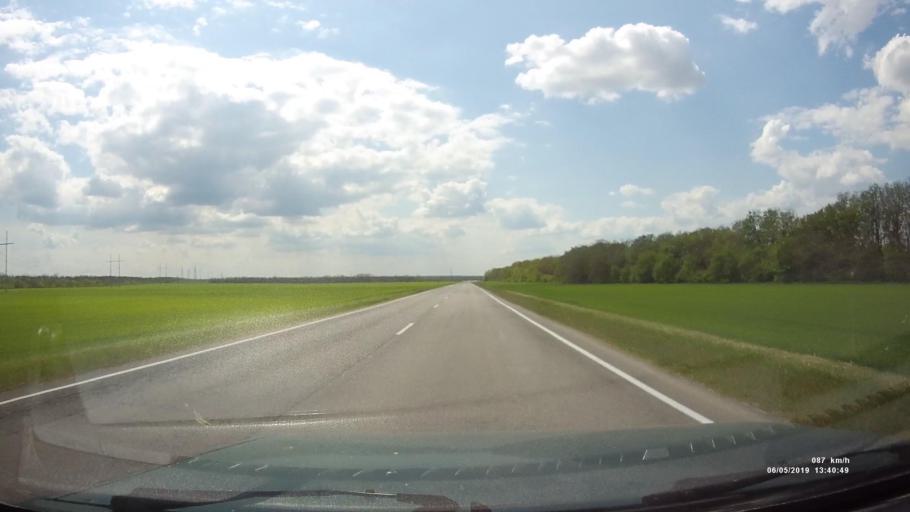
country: RU
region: Rostov
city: Ust'-Donetskiy
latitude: 47.6662
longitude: 40.6884
